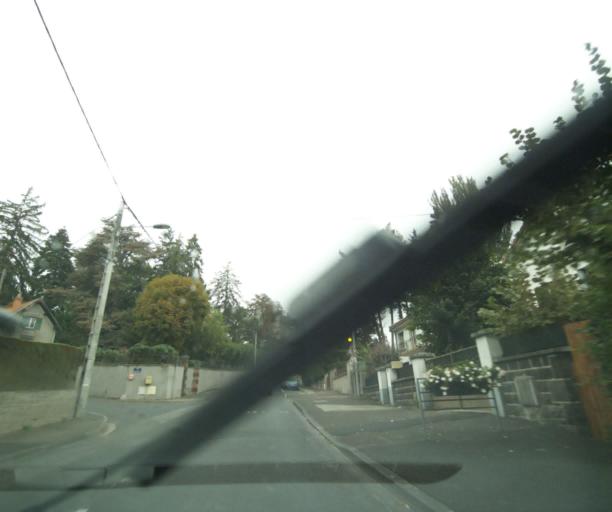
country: FR
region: Auvergne
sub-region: Departement du Puy-de-Dome
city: Durtol
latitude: 45.7896
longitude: 3.0543
